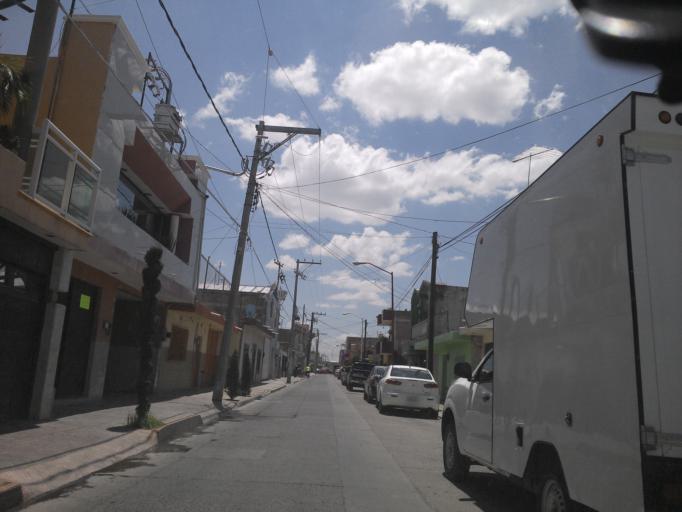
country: MX
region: Guanajuato
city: San Francisco del Rincon
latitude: 21.0110
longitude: -101.8537
